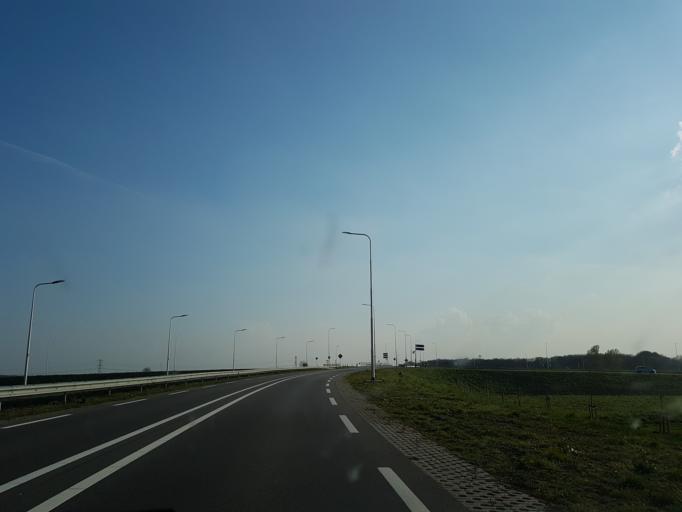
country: NL
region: Overijssel
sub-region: Gemeente Raalte
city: Heino
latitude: 52.4849
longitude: 6.1787
